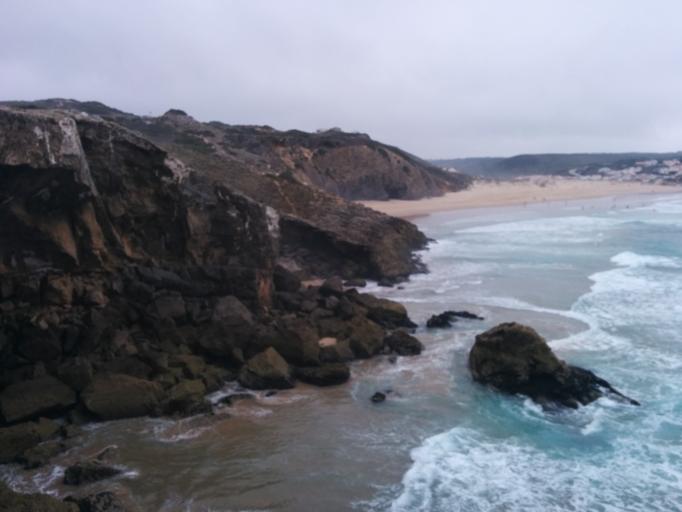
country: PT
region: Faro
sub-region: Aljezur
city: Aljezur
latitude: 37.3465
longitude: -8.8509
